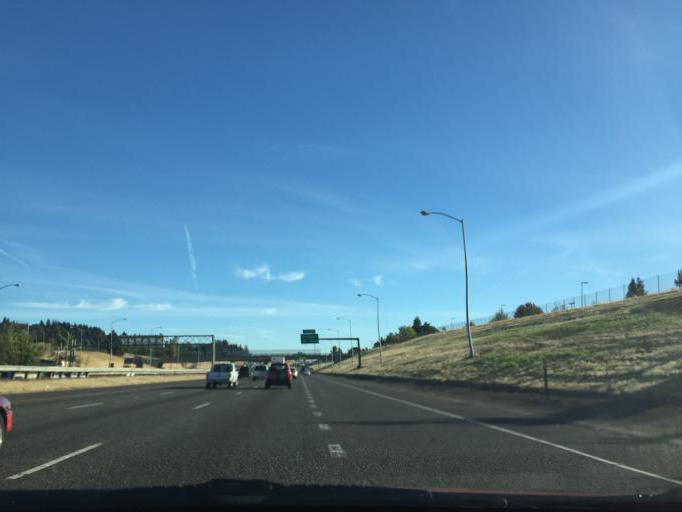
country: US
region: Oregon
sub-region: Multnomah County
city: Lents
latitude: 45.5136
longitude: -122.5655
